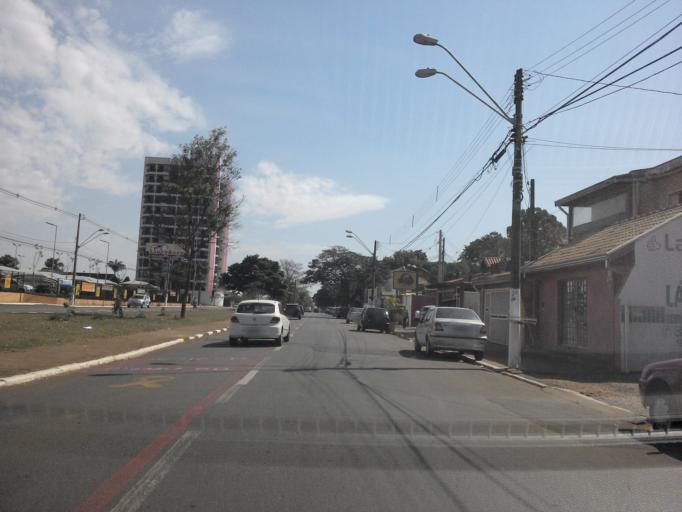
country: BR
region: Sao Paulo
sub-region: Sumare
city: Sumare
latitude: -22.8304
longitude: -47.2657
